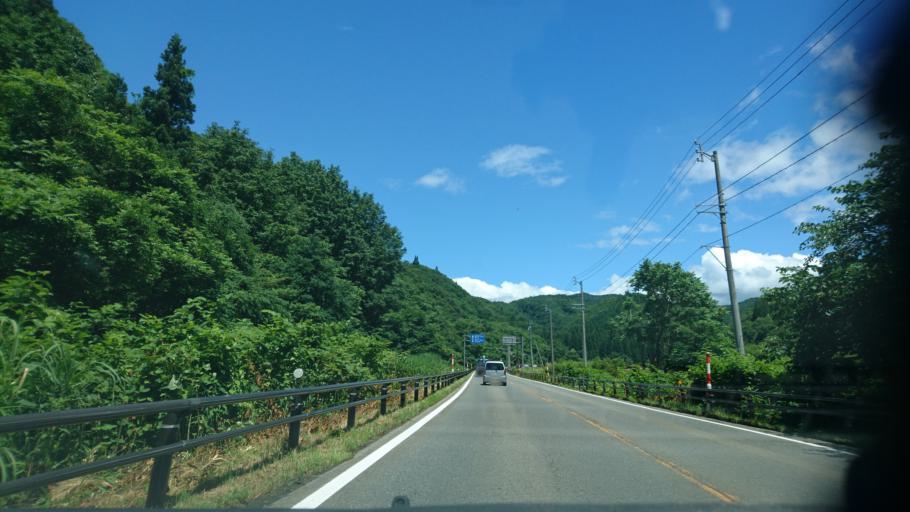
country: JP
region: Akita
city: Kakunodatemachi
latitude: 39.6558
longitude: 140.6723
